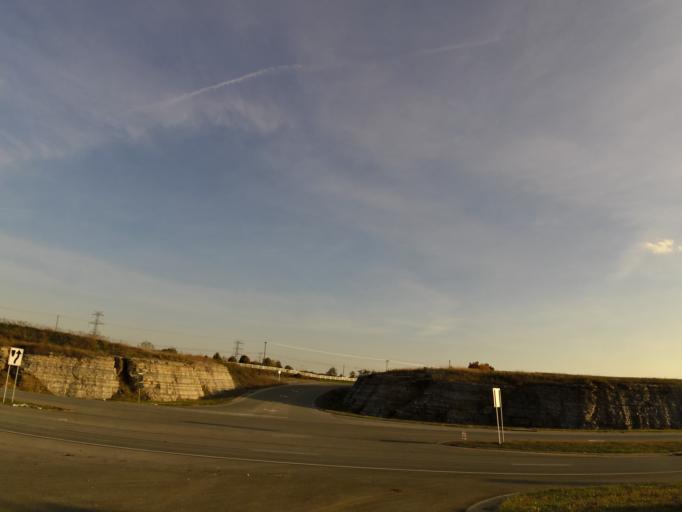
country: US
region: Kentucky
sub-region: Garrard County
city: Lancaster
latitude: 37.7028
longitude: -84.6628
